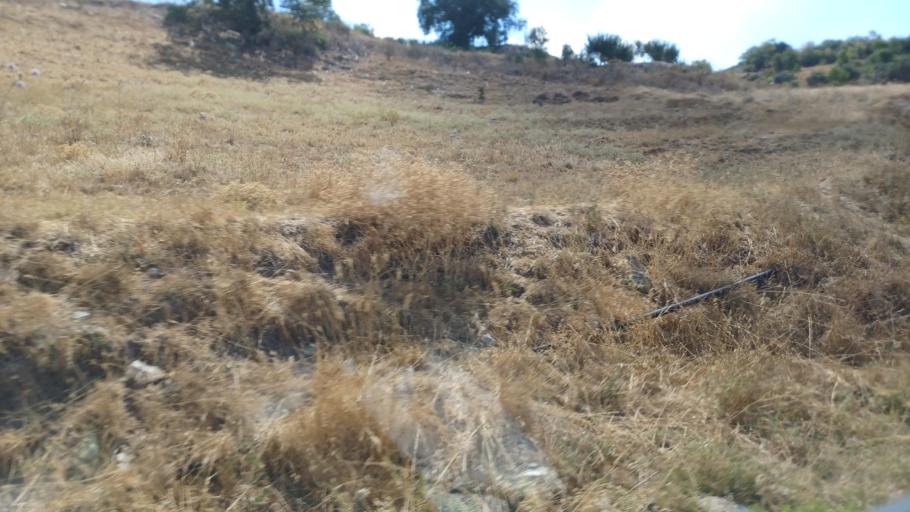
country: CY
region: Pafos
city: Mesogi
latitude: 34.8871
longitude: 32.6112
